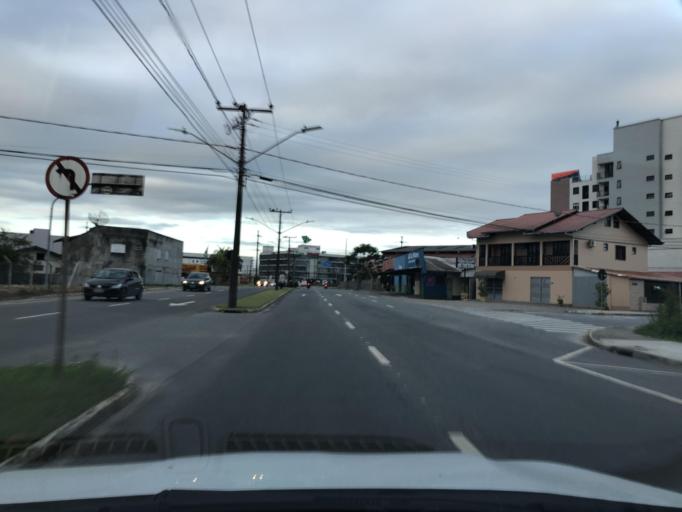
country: BR
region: Santa Catarina
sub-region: Joinville
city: Joinville
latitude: -26.2663
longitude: -48.8621
